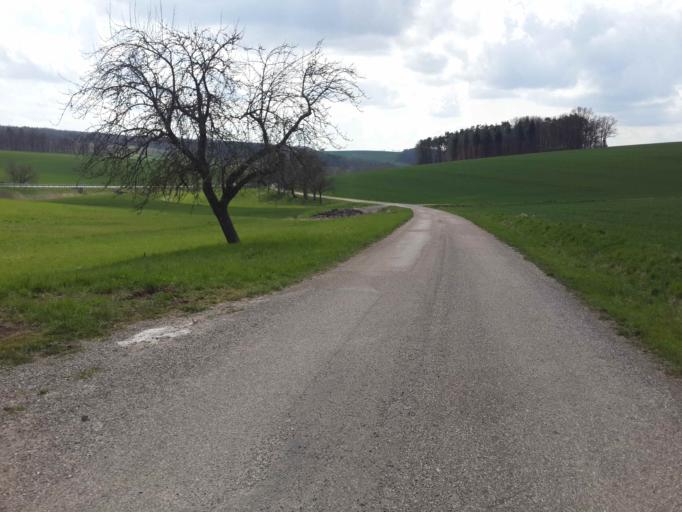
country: DE
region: Baden-Wuerttemberg
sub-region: Regierungsbezirk Stuttgart
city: Dorzbach
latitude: 49.4160
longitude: 9.7364
